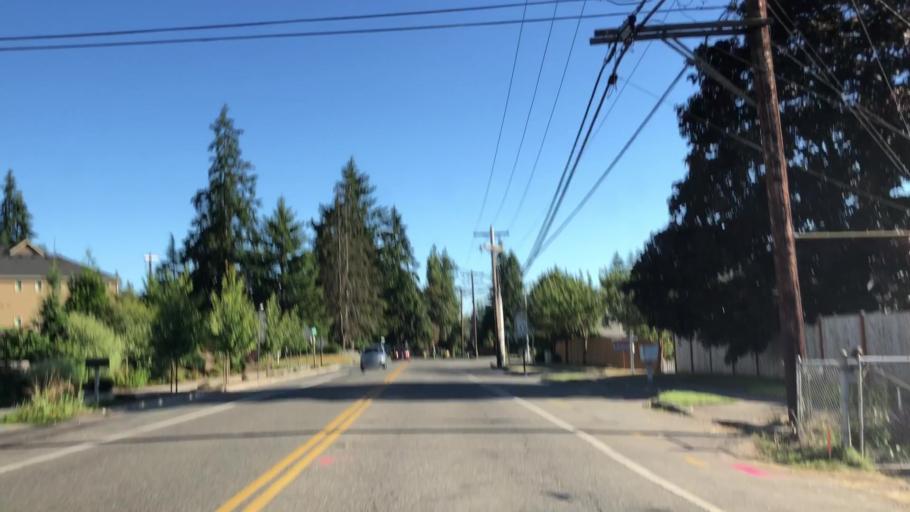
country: US
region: Washington
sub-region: Snohomish County
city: Alderwood Manor
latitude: 47.8116
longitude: -122.2441
